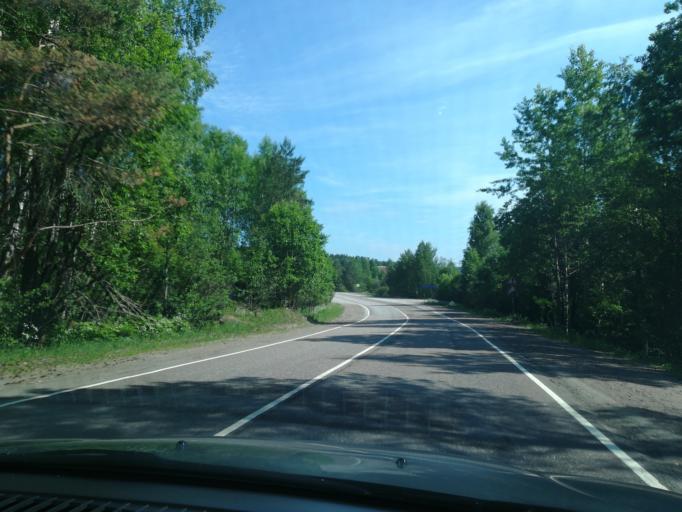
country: RU
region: Leningrad
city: Lesogorskiy
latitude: 60.9139
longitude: 28.8878
